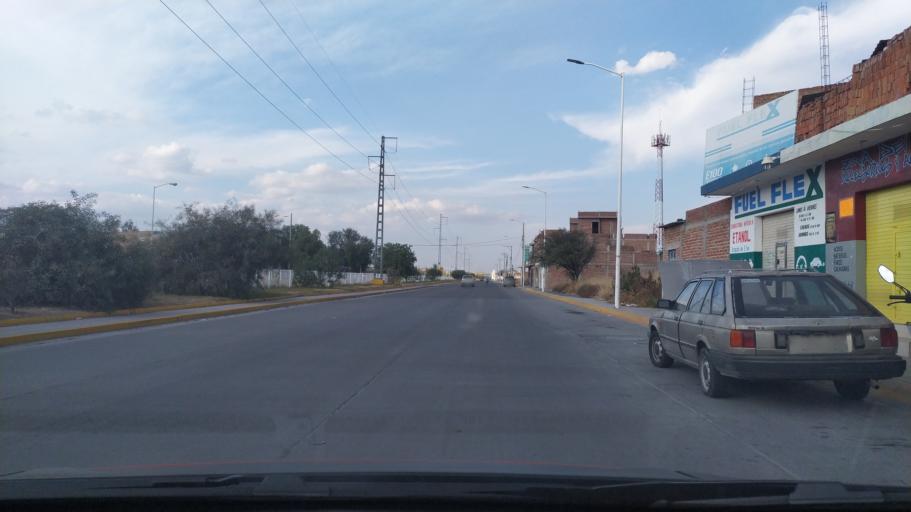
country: MX
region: Guanajuato
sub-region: Purisima del Rincon
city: Monte Grande
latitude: 21.0083
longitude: -101.8699
